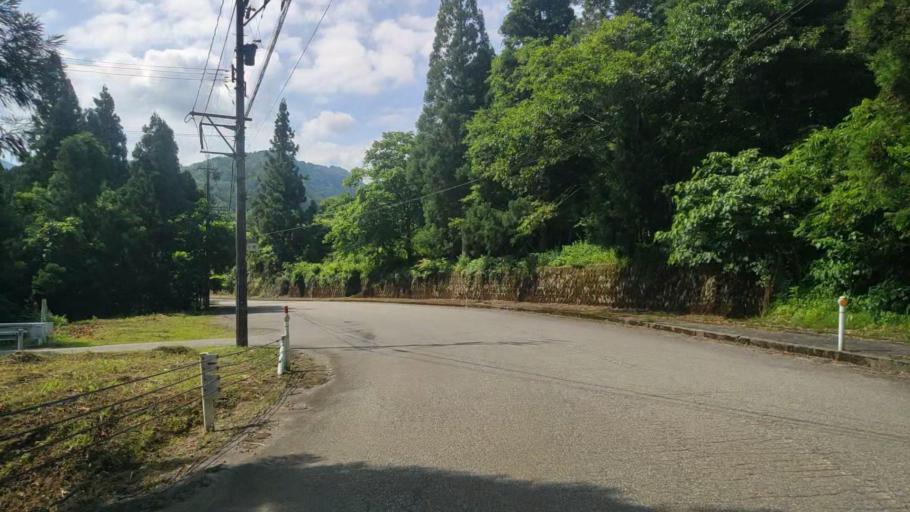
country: JP
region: Ishikawa
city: Komatsu
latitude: 36.3014
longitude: 136.5280
